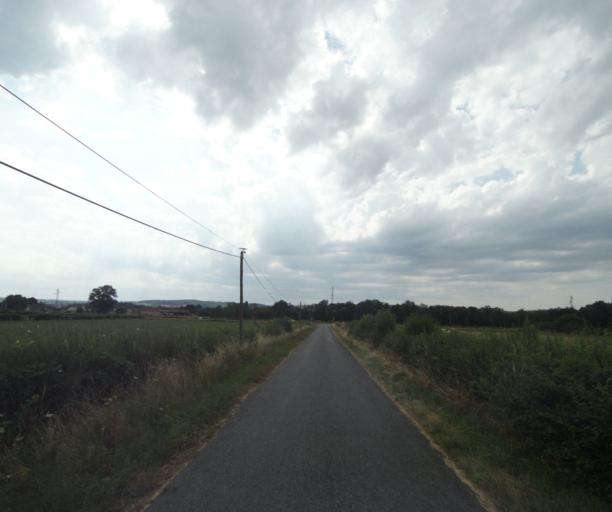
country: FR
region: Bourgogne
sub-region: Departement de Saone-et-Loire
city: Gueugnon
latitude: 46.6154
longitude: 4.0810
